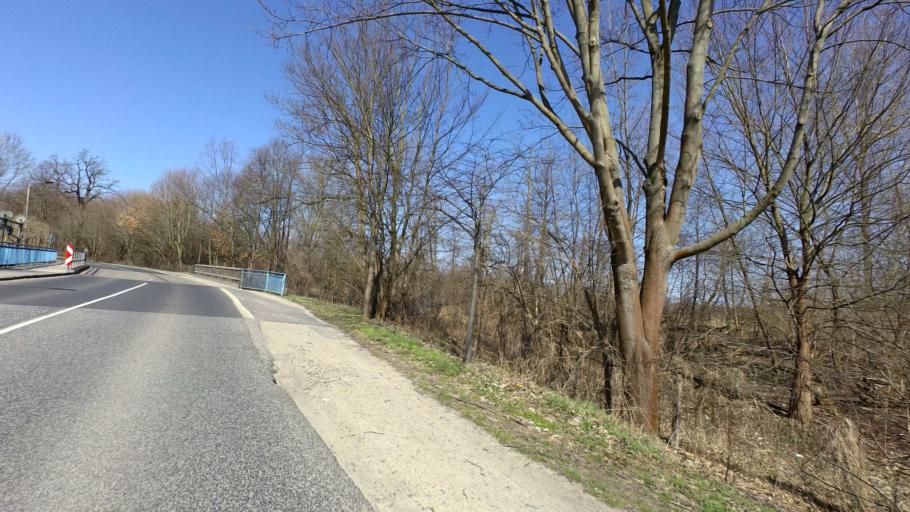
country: DE
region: Brandenburg
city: Oranienburg
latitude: 52.7743
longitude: 13.2463
